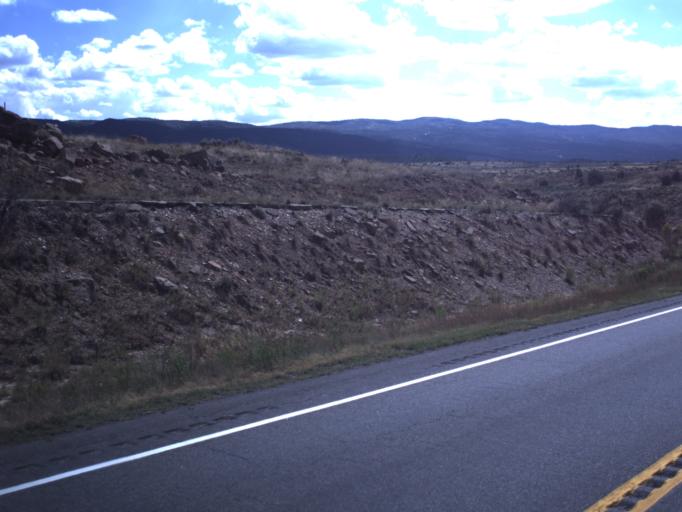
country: US
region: Utah
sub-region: Duchesne County
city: Duchesne
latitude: 40.2101
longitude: -110.7619
